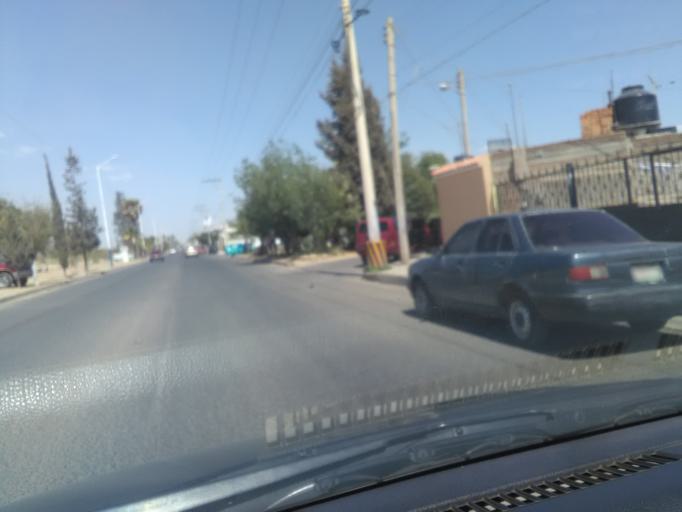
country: MX
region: Durango
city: Victoria de Durango
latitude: 24.0442
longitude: -104.6456
